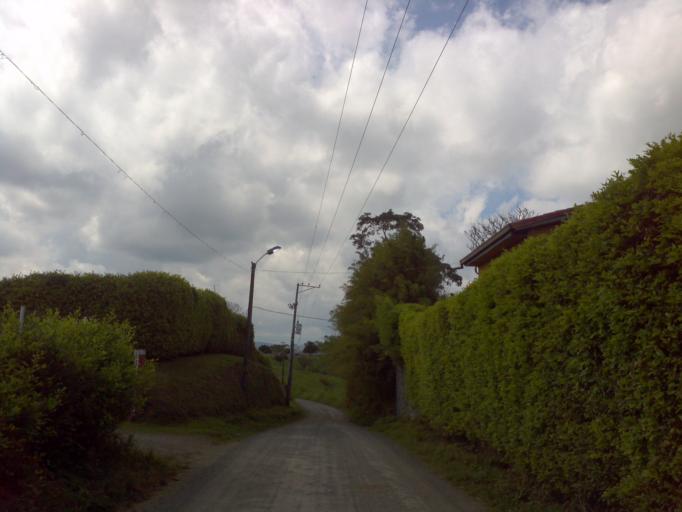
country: CO
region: Valle del Cauca
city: Ulloa
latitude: 4.7361
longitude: -75.7058
